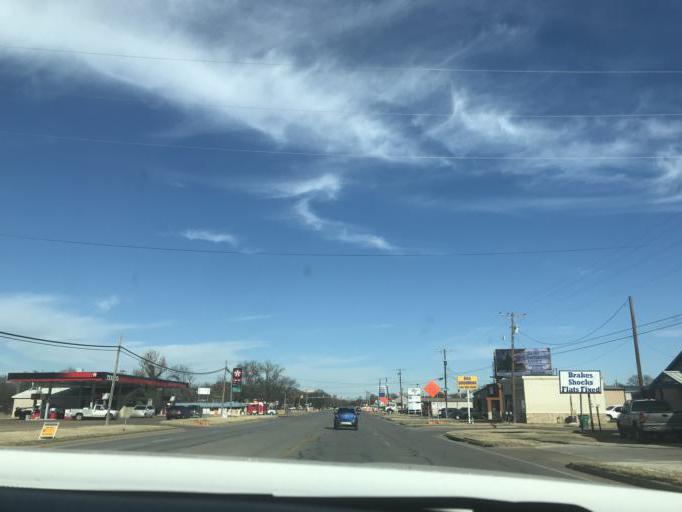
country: US
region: Texas
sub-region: Erath County
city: Stephenville
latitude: 32.2308
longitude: -98.2127
